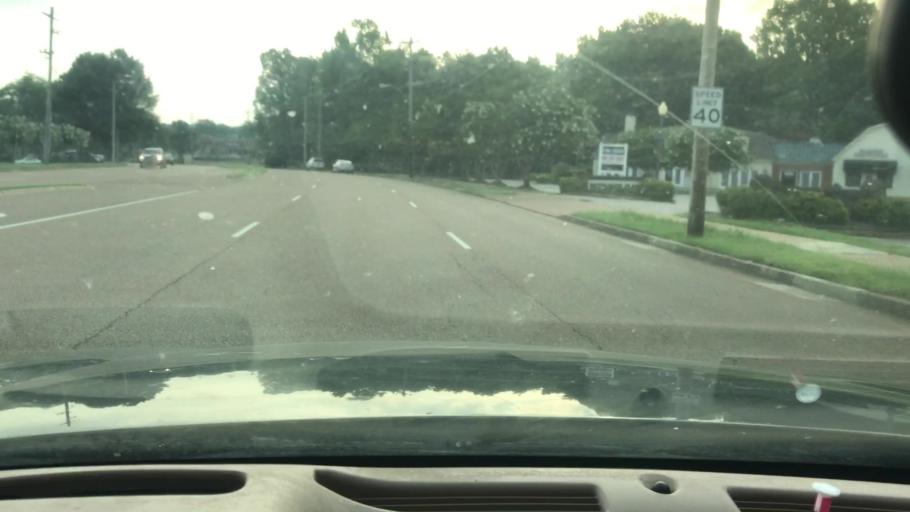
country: US
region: Tennessee
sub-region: Shelby County
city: Bartlett
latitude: 35.2009
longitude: -89.8667
